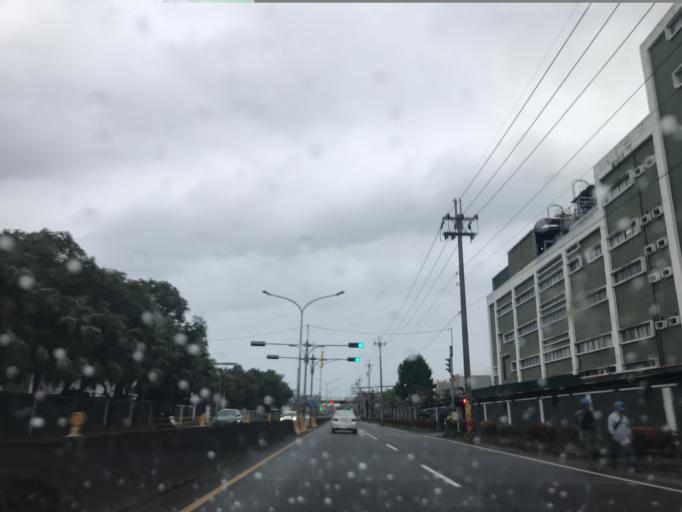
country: TW
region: Taiwan
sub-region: Hsinchu
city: Zhubei
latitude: 24.8257
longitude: 121.0562
